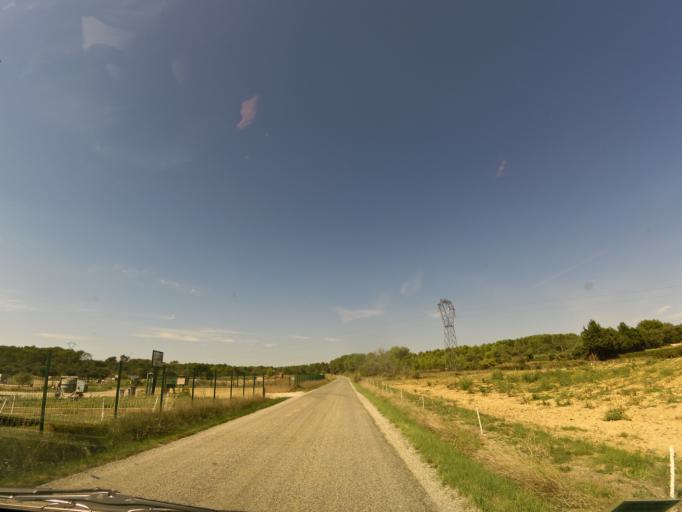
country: FR
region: Languedoc-Roussillon
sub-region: Departement du Gard
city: Uchaud
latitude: 43.7671
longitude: 4.2494
